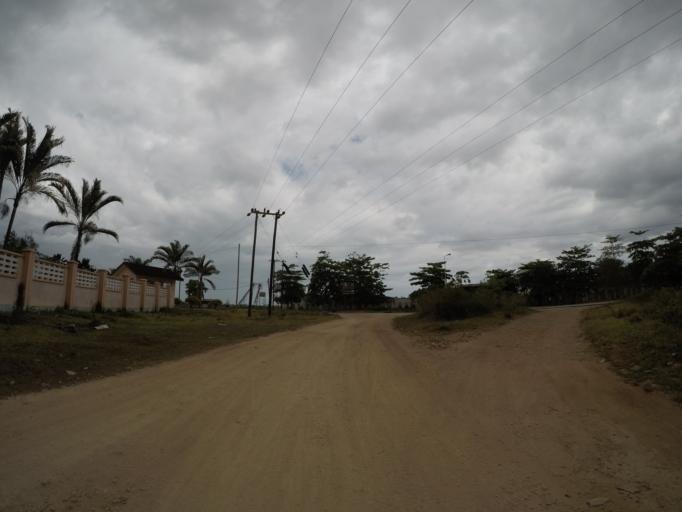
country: TZ
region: Zanzibar Central/South
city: Koani
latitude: -6.1983
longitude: 39.3089
